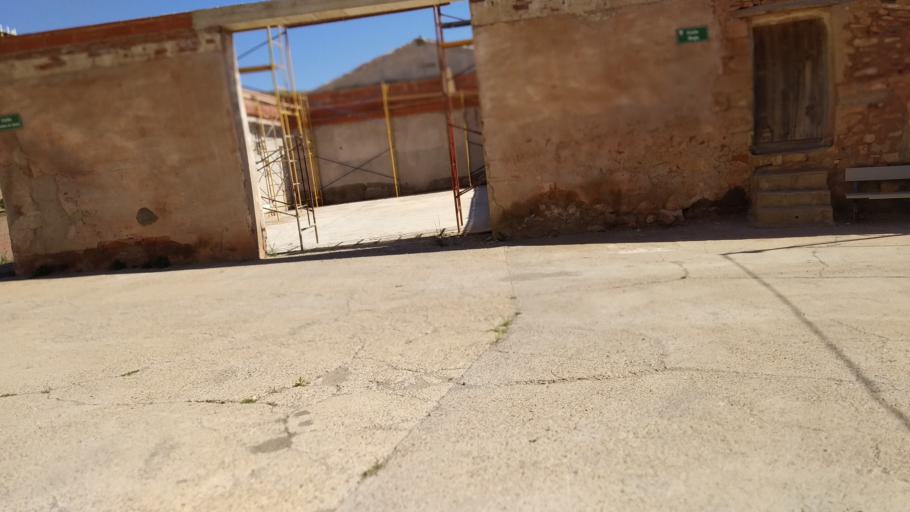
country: ES
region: Aragon
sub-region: Provincia de Teruel
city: Monforte de Moyuela
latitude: 41.0557
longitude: -1.0148
